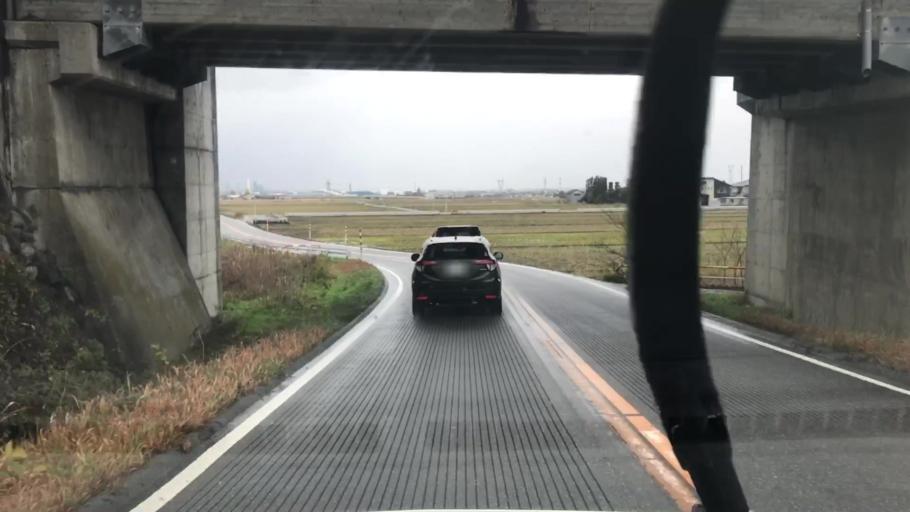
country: JP
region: Toyama
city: Toyama-shi
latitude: 36.6724
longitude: 137.2865
